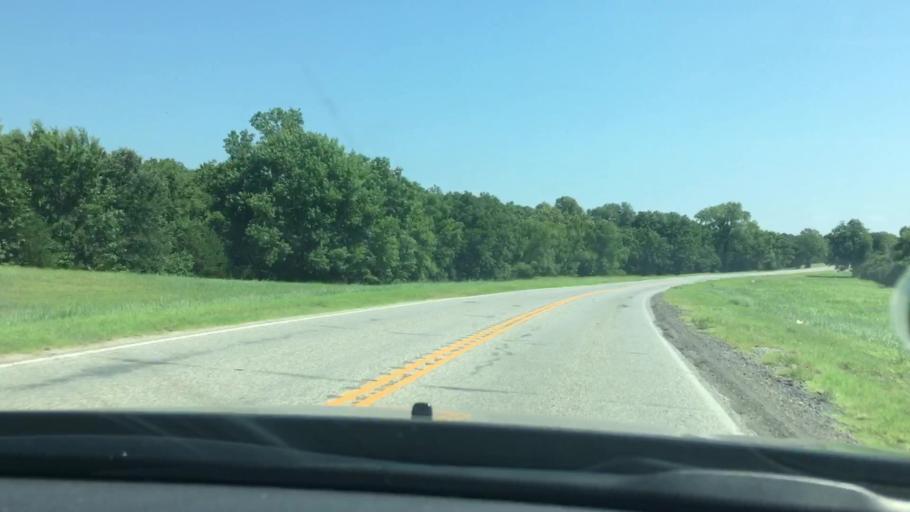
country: US
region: Oklahoma
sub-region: Johnston County
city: Tishomingo
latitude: 34.2367
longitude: -96.6138
